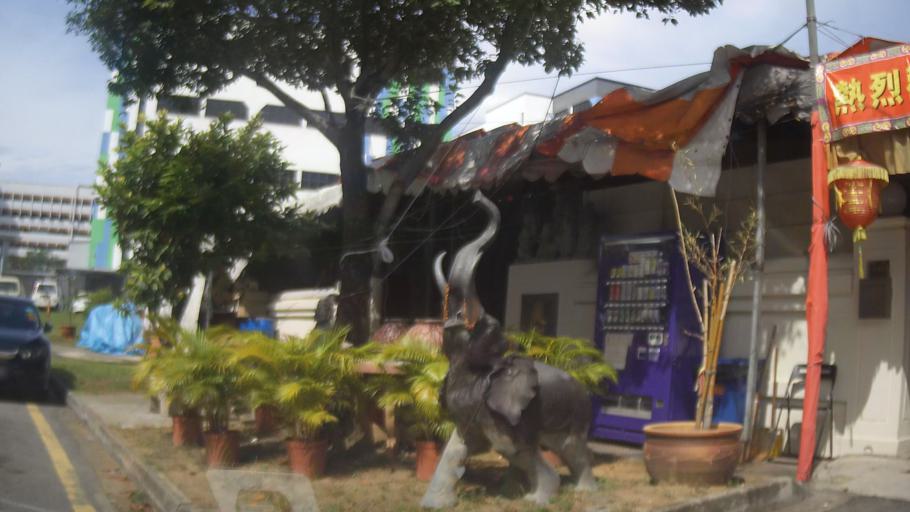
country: SG
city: Singapore
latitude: 1.3282
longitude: 103.8910
